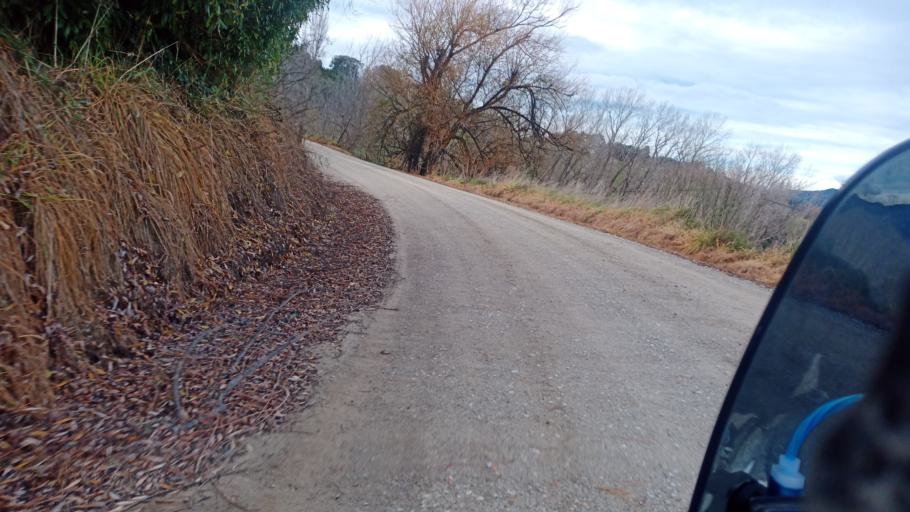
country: NZ
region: Gisborne
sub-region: Gisborne District
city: Gisborne
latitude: -38.3853
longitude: 177.9577
